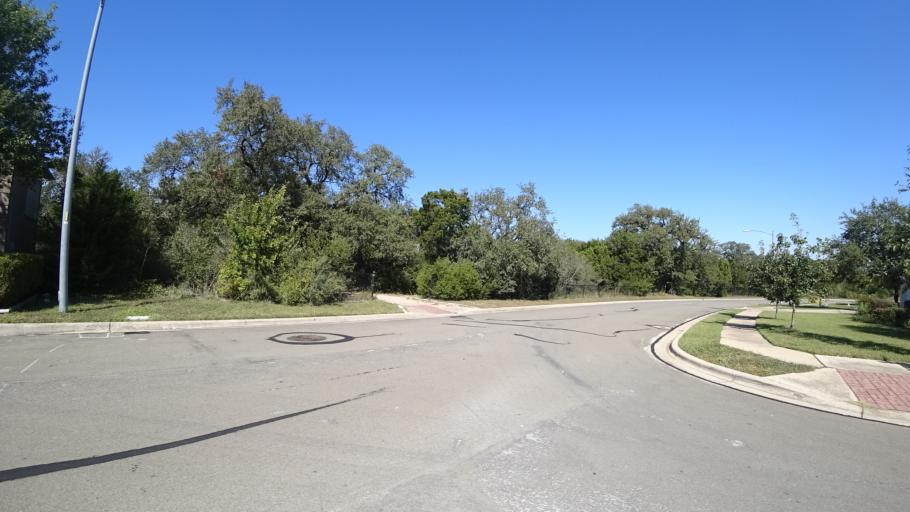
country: US
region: Texas
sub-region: Travis County
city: Shady Hollow
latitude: 30.2066
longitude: -97.8671
